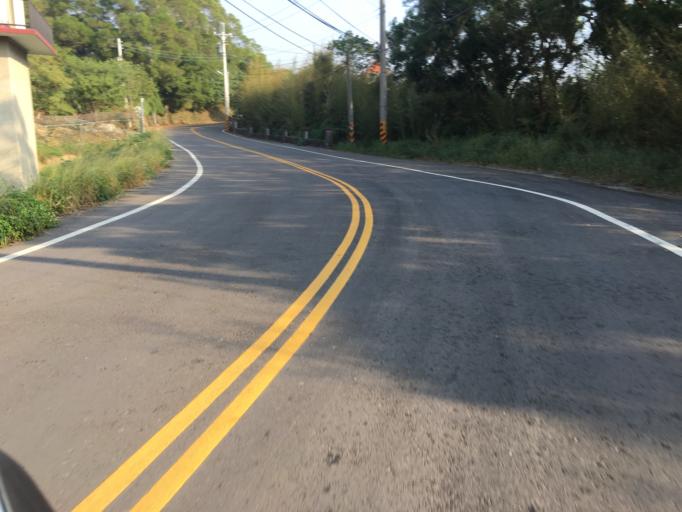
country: TW
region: Taiwan
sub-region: Hsinchu
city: Hsinchu
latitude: 24.7482
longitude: 121.0346
